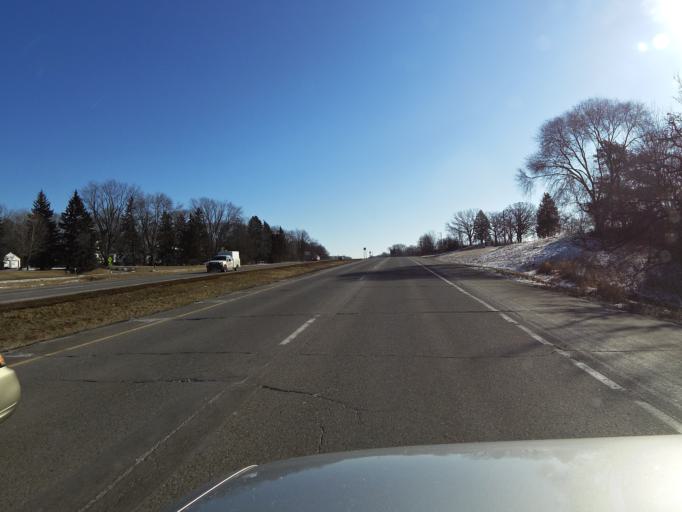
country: US
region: Minnesota
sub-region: Dakota County
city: Mendota Heights
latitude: 44.8836
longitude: -93.1192
